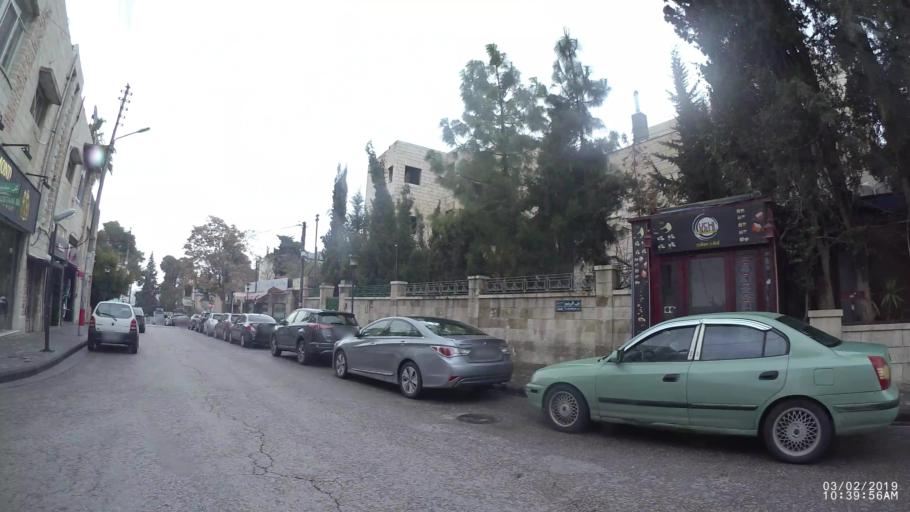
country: JO
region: Amman
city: Amman
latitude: 31.9492
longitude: 35.9286
